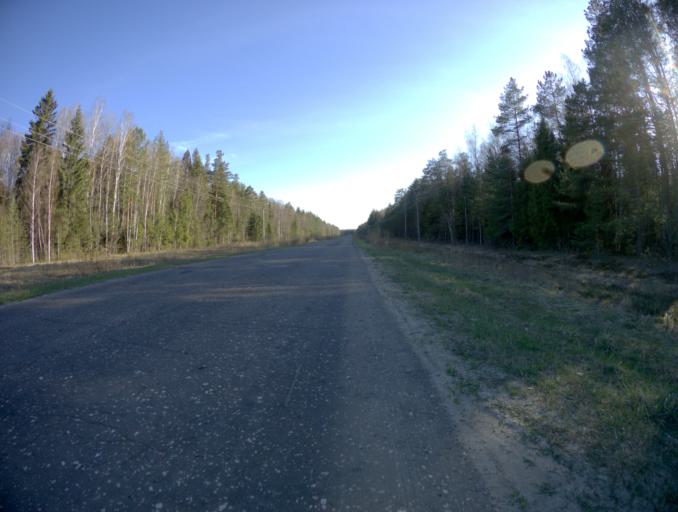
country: RU
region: Vladimir
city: Mezinovskiy
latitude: 55.6192
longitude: 40.3806
